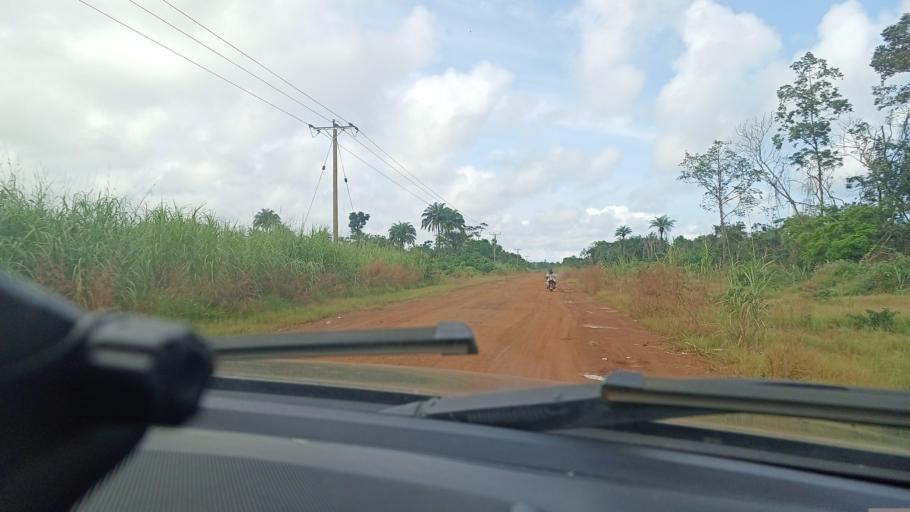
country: LR
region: Grand Cape Mount
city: Robertsport
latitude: 6.6835
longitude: -11.1279
